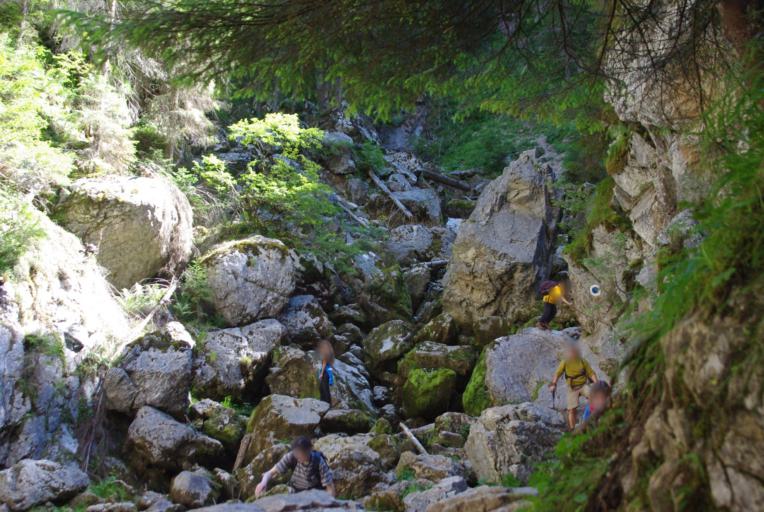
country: RO
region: Alba
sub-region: Comuna Arieseni
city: Arieseni
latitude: 46.5644
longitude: 22.7029
